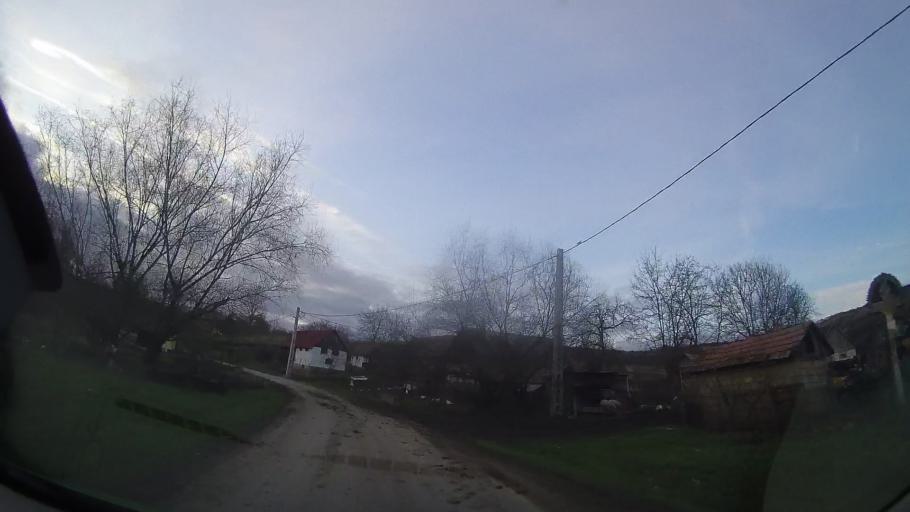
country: RO
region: Cluj
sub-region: Comuna Mociu
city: Mociu
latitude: 46.8568
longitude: 24.0422
